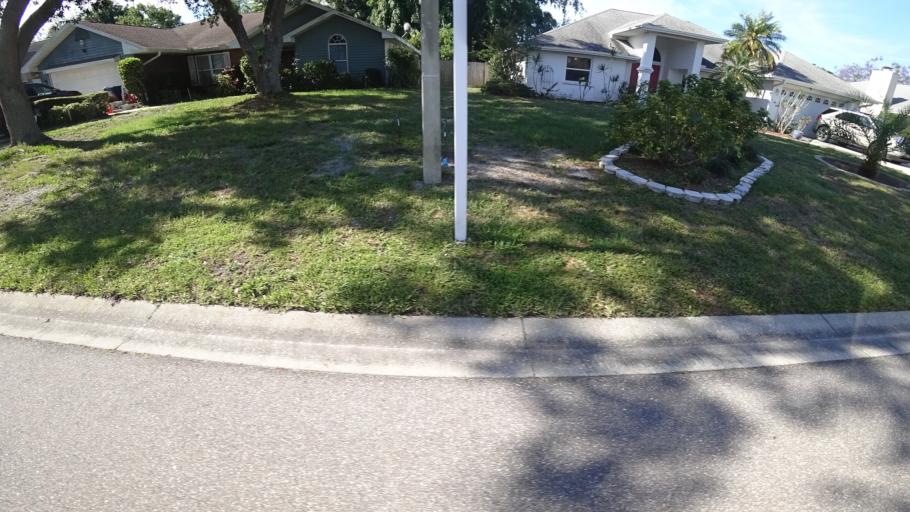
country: US
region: Florida
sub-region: Manatee County
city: West Bradenton
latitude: 27.5104
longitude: -82.6508
